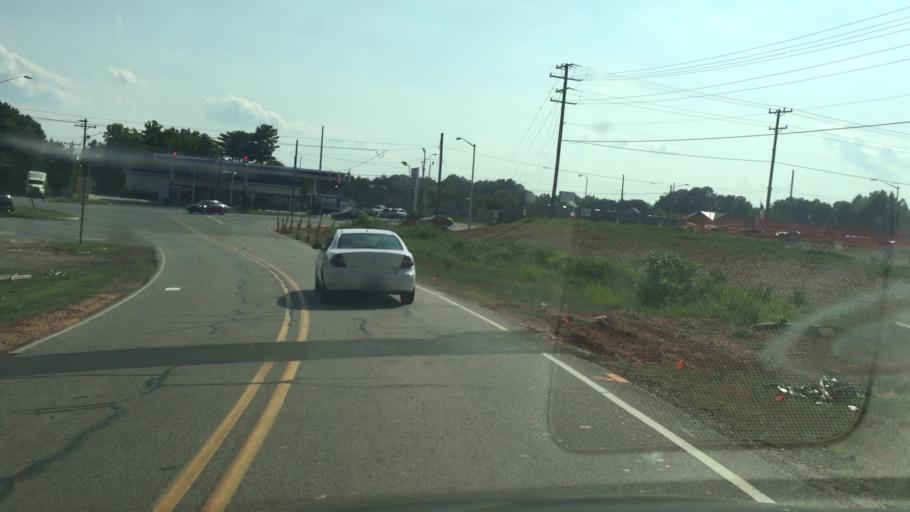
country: US
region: North Carolina
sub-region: Rockingham County
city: Reidsville
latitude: 36.3263
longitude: -79.6398
